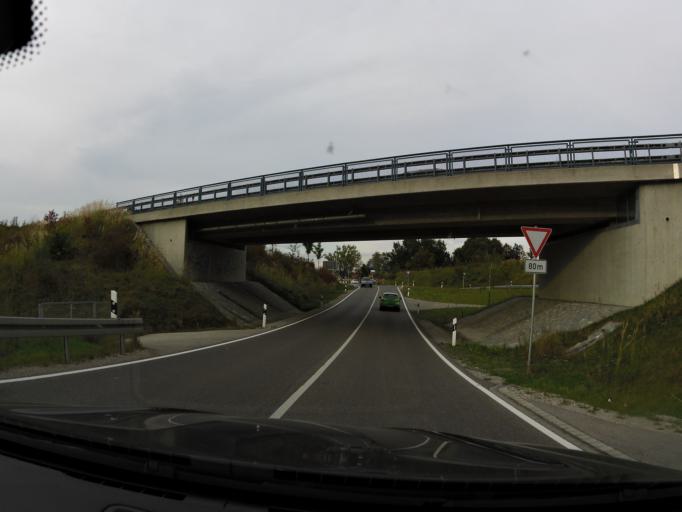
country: DE
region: Bavaria
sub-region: Upper Bavaria
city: Puchheim
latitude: 48.1479
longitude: 11.3385
